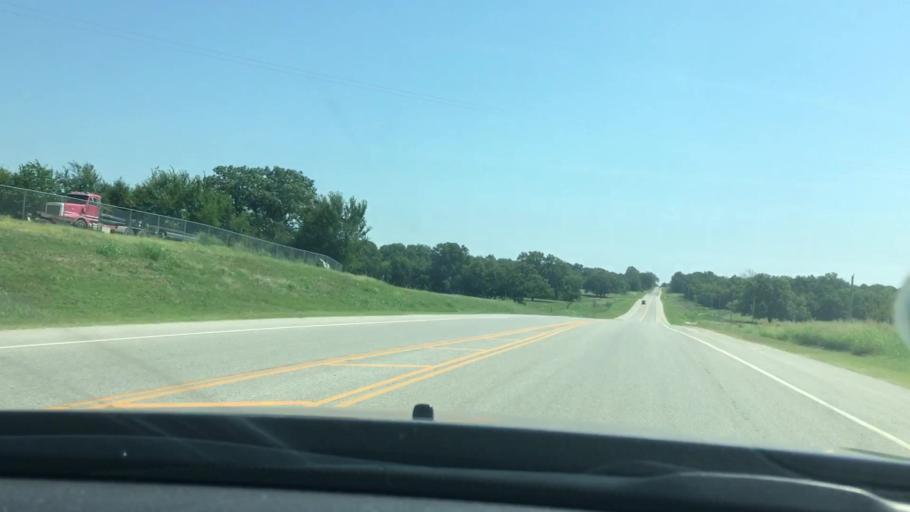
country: US
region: Oklahoma
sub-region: Johnston County
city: Tishomingo
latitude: 34.2741
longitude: -96.5483
